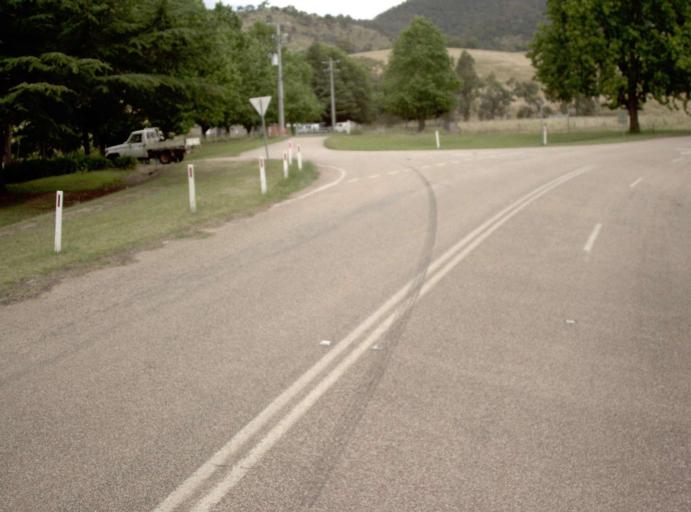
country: AU
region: Victoria
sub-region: East Gippsland
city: Bairnsdale
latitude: -37.4697
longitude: 147.2540
